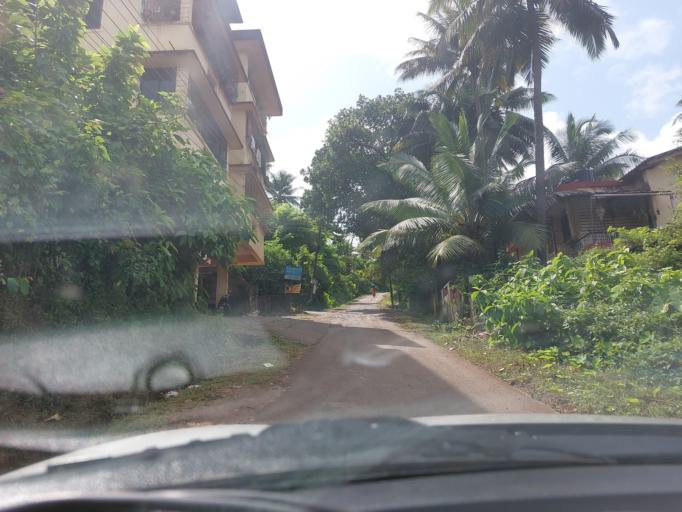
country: IN
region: Goa
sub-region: North Goa
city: Queula
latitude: 15.3991
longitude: 73.9980
